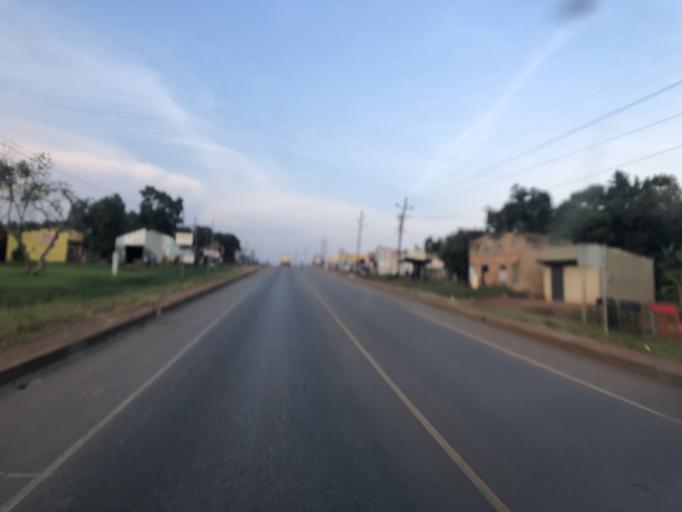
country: UG
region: Central Region
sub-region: Mpigi District
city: Mpigi
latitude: 0.2058
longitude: 32.3128
